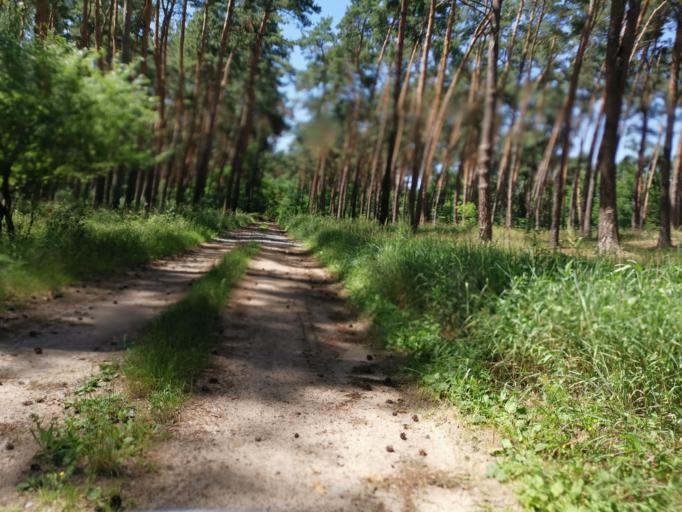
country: CZ
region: South Moravian
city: Bzenec
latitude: 48.9649
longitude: 17.2540
